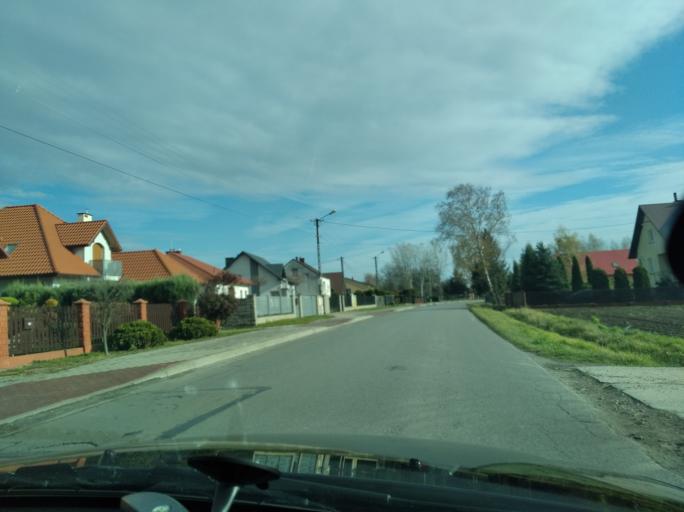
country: PL
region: Subcarpathian Voivodeship
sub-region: Powiat ropczycko-sedziszowski
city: Ostrow
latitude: 50.1010
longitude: 21.6018
